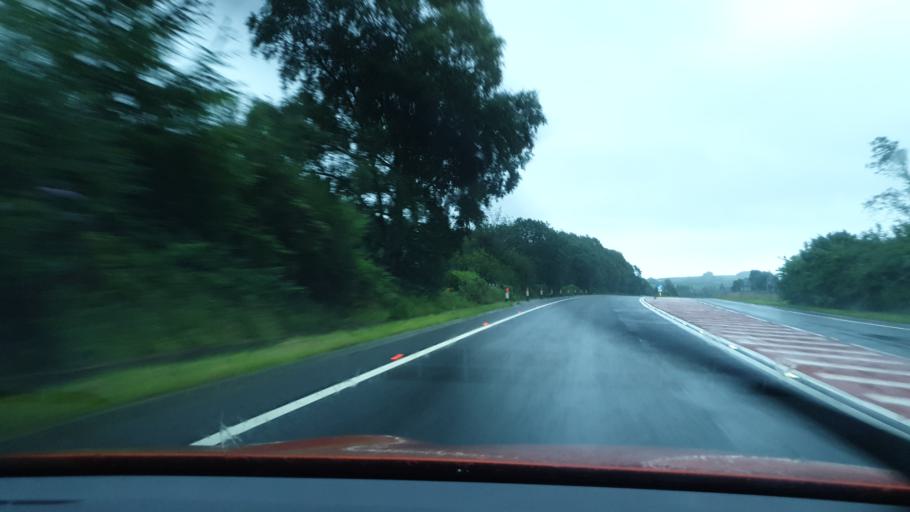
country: GB
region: England
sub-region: Cumbria
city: Grange-over-Sands
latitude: 54.2546
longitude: -2.9438
